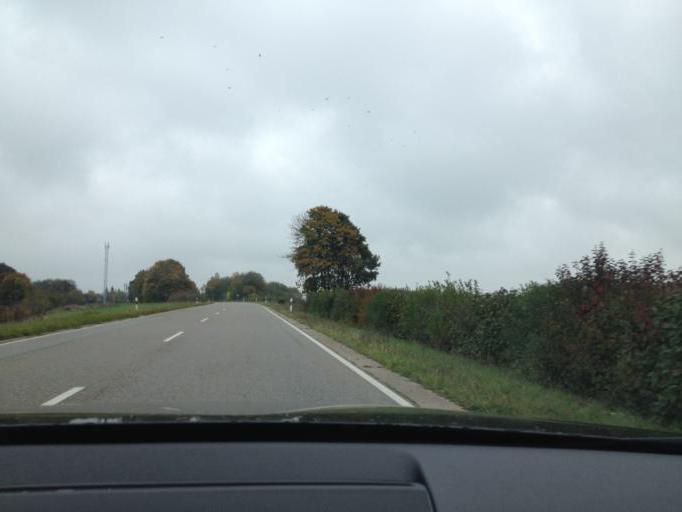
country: DE
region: Rheinland-Pfalz
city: Rieschweiler-Muhlbach
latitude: 49.2197
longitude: 7.5062
